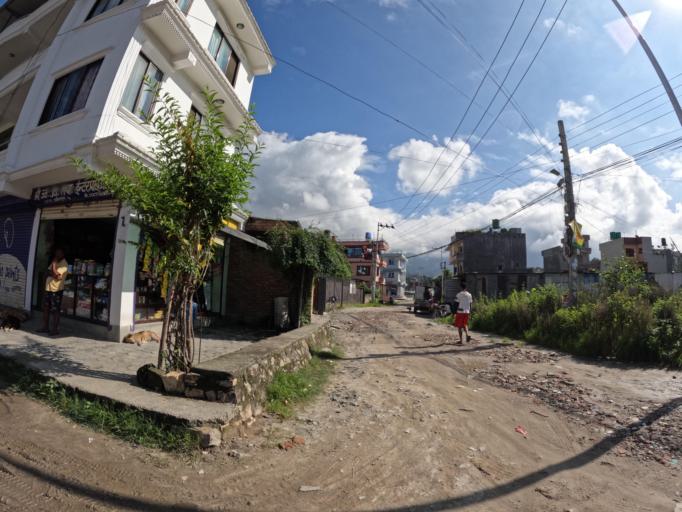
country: NP
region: Central Region
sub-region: Bagmati Zone
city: Kathmandu
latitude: 27.7587
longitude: 85.3358
